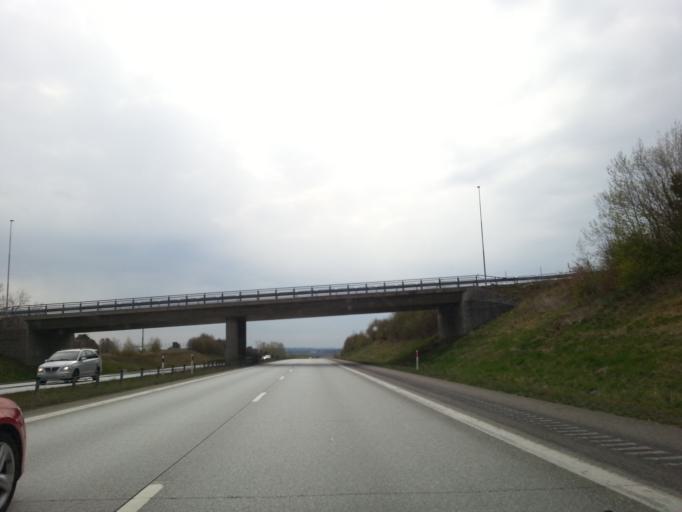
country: SE
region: Halland
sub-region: Falkenbergs Kommun
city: Falkenberg
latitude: 56.9244
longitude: 12.5351
